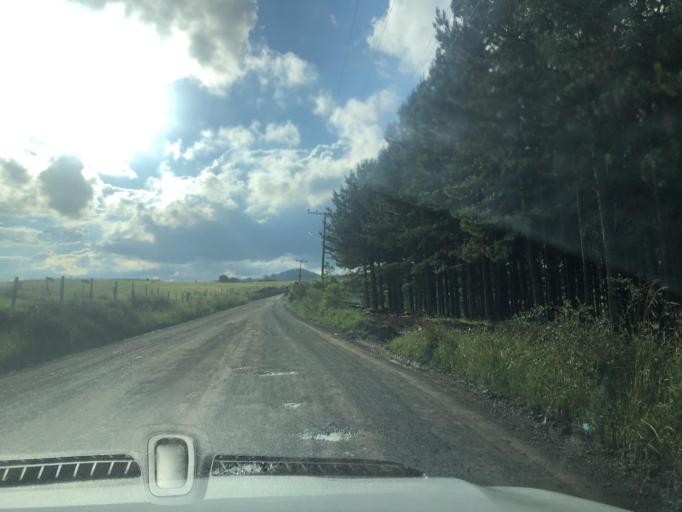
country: BR
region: Santa Catarina
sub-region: Lages
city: Lages
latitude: -27.7915
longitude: -50.3215
